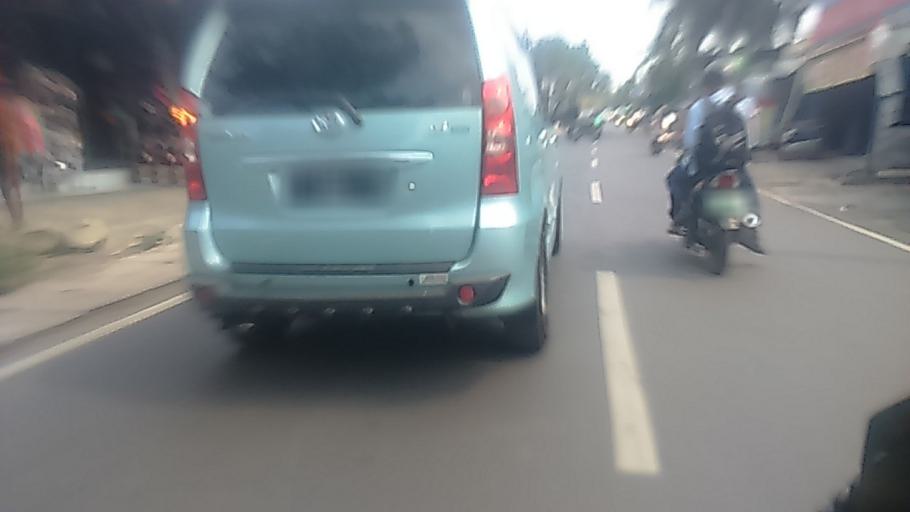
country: ID
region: West Java
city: Depok
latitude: -6.3397
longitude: 106.8049
